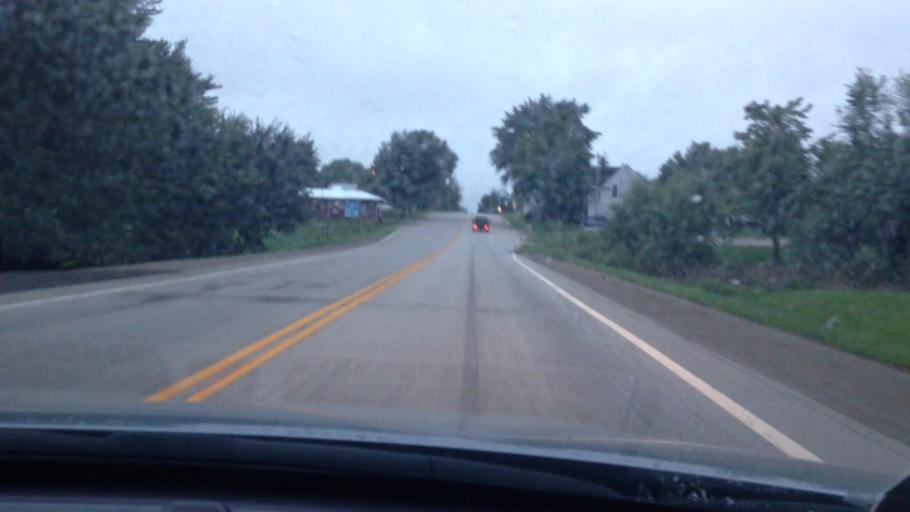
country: US
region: Kansas
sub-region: Brown County
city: Horton
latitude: 39.6739
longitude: -95.5272
